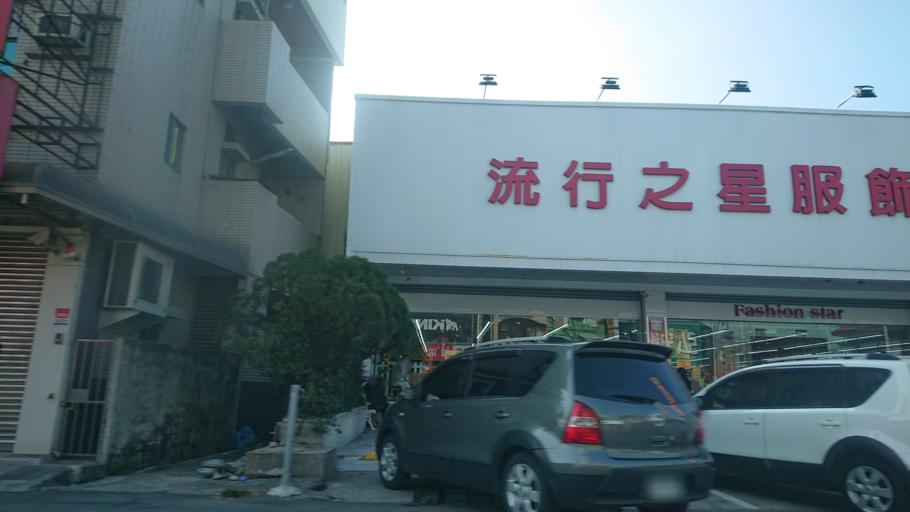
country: TW
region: Taiwan
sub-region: Chiayi
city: Taibao
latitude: 23.4620
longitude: 120.2411
